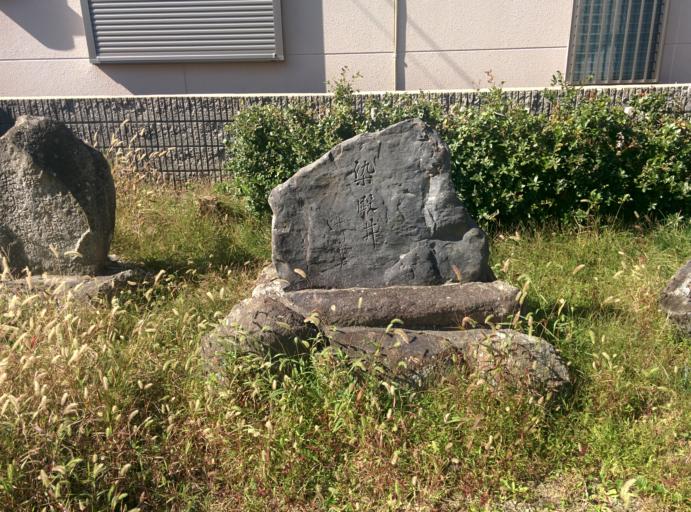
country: JP
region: Osaka
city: Ikeda
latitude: 34.8170
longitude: 135.4266
